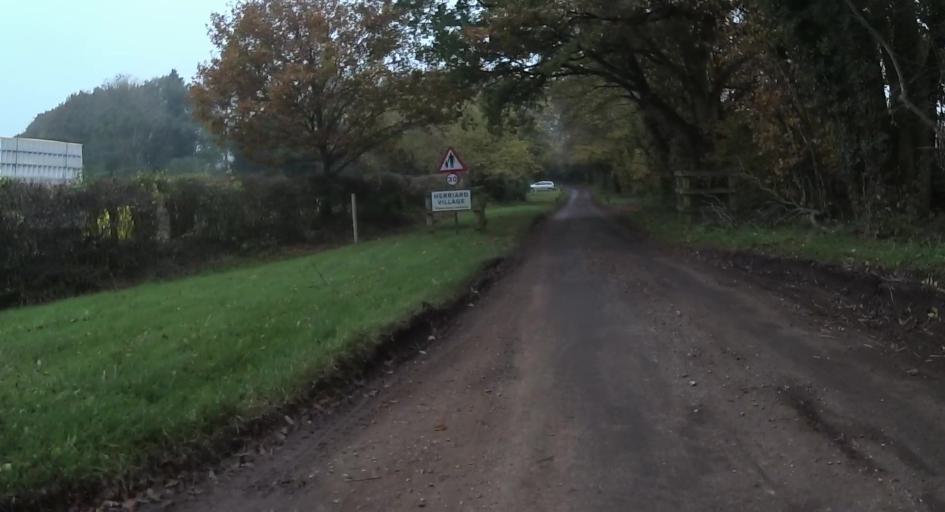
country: GB
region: England
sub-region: Hampshire
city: Old Basing
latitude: 51.2028
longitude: -1.0382
